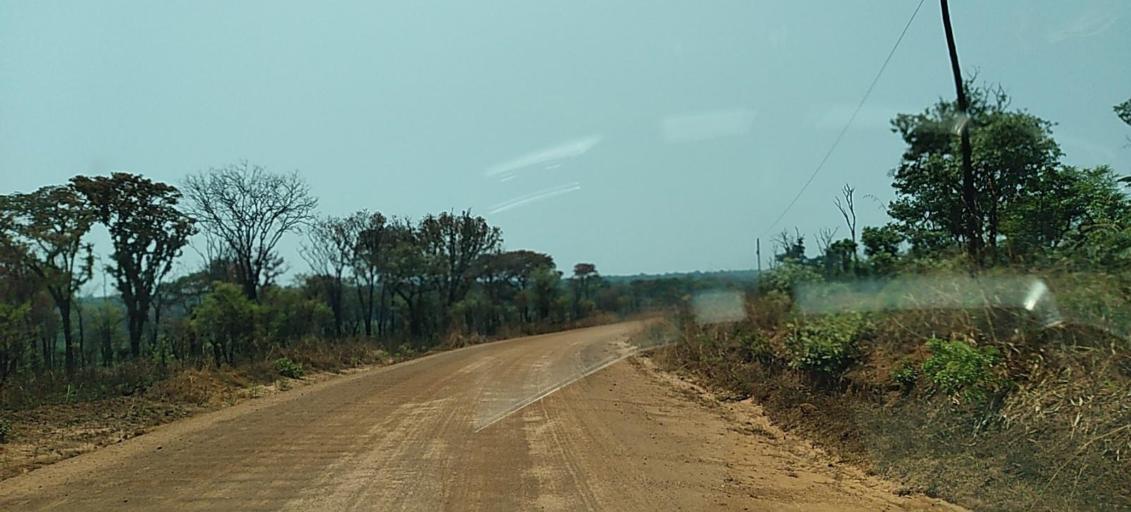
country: ZM
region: North-Western
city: Kansanshi
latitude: -11.9812
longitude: 26.7875
